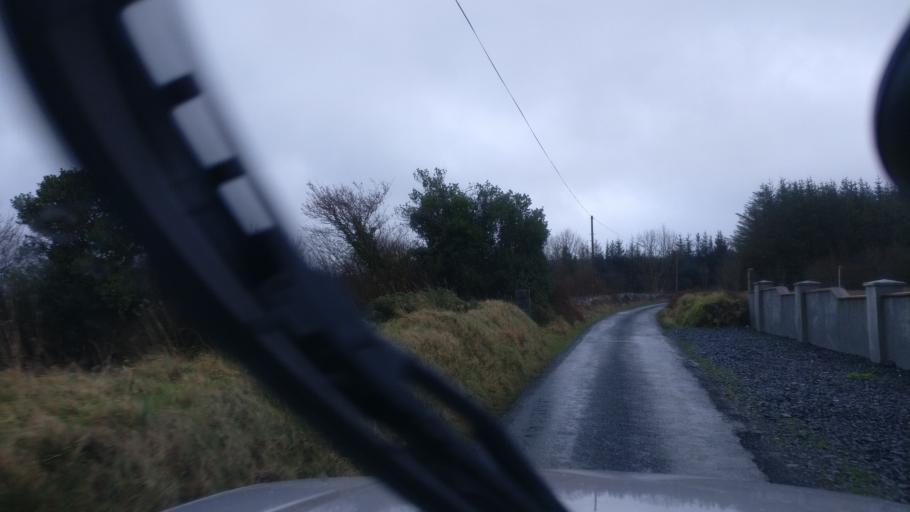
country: IE
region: Connaught
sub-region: County Galway
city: Loughrea
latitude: 53.1501
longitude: -8.6176
